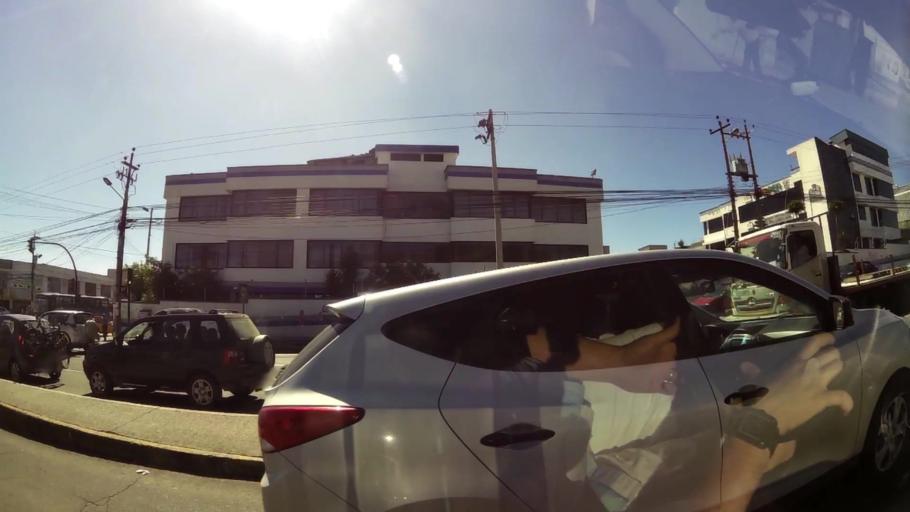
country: EC
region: Pichincha
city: Quito
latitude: -0.1290
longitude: -78.4712
